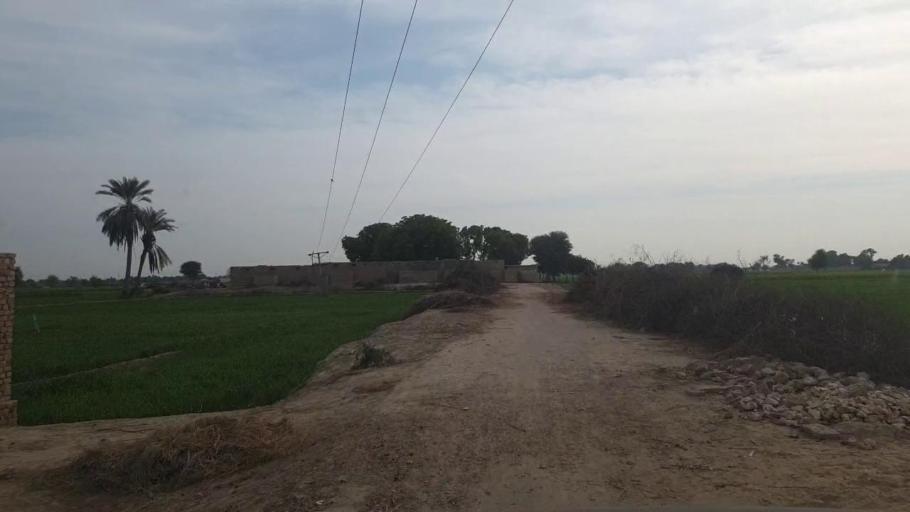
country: PK
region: Sindh
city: Shahpur Chakar
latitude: 26.1159
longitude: 68.5252
